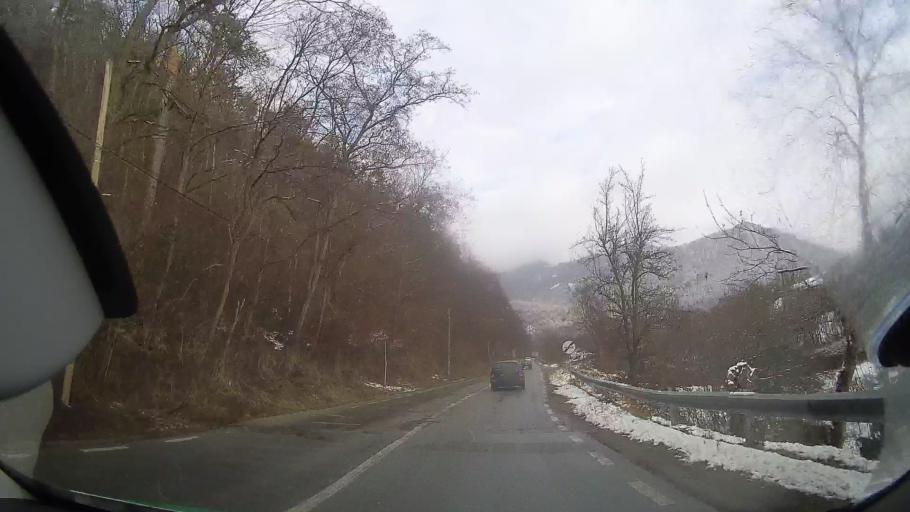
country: RO
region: Alba
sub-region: Oras Baia de Aries
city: Baia de Aries
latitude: 46.4019
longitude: 23.3221
